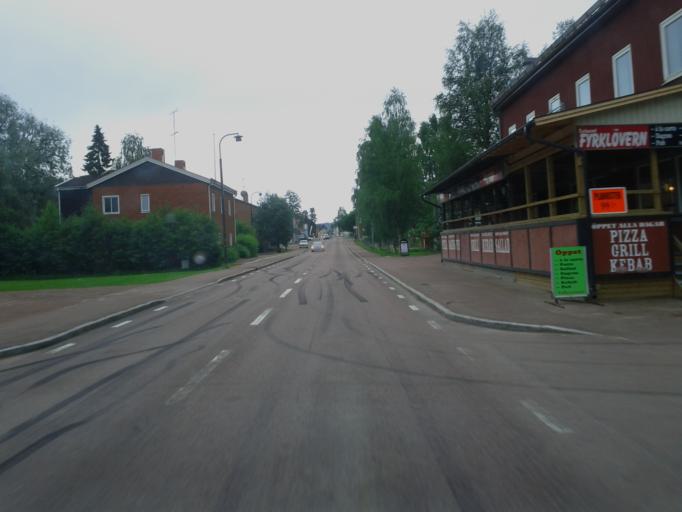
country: SE
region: Dalarna
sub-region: Alvdalens Kommun
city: AElvdalen
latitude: 61.2332
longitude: 14.0355
